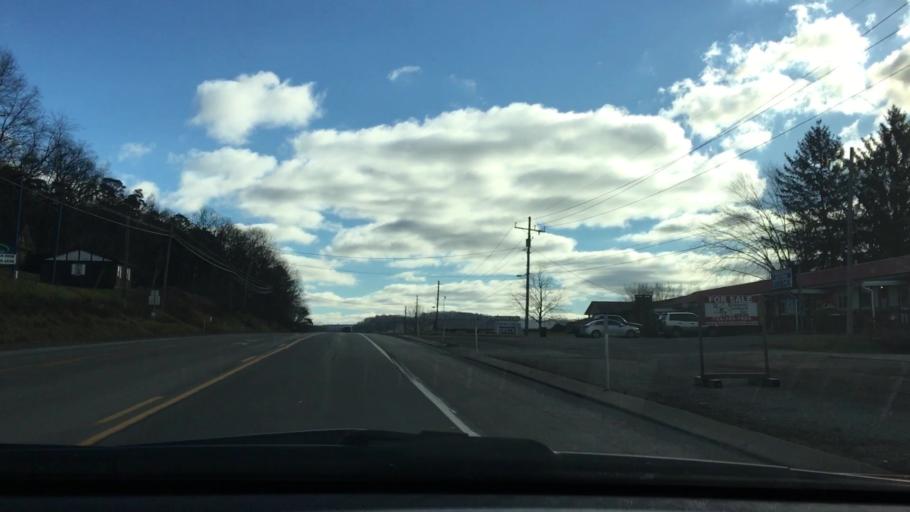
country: US
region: Pennsylvania
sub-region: Indiana County
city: Indiana
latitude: 40.6570
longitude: -79.3002
